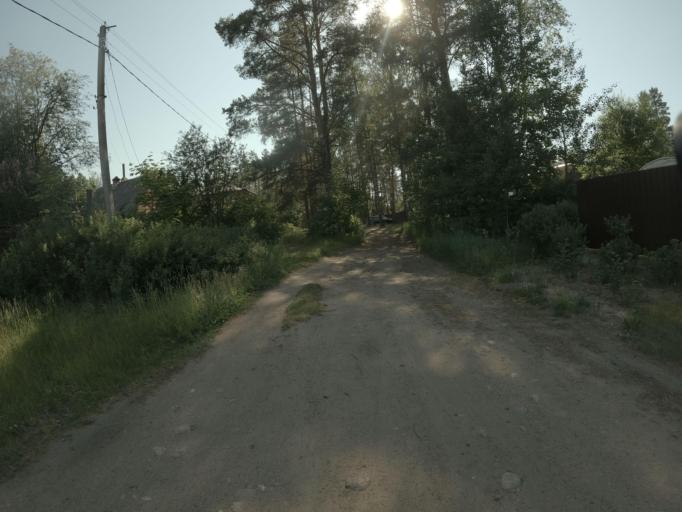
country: RU
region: Leningrad
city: Yakovlevo
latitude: 60.4658
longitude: 29.2806
